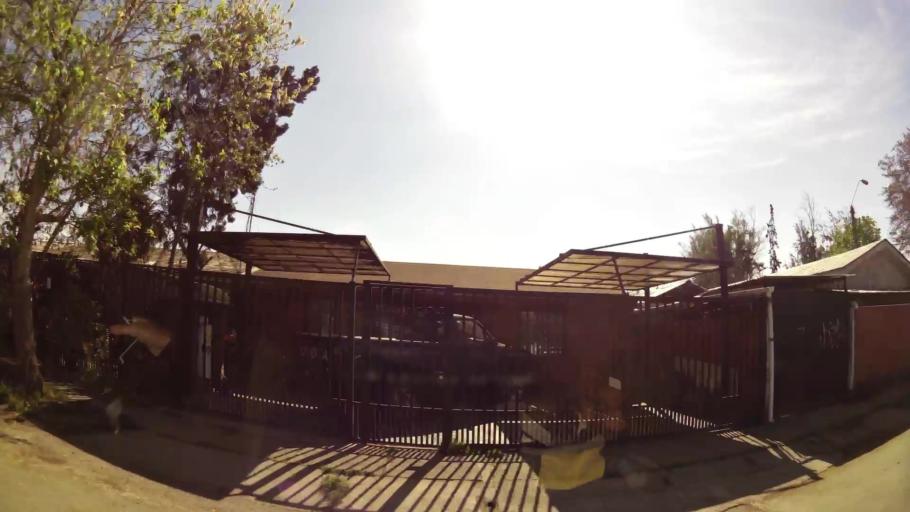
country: CL
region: Santiago Metropolitan
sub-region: Provincia de Santiago
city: Villa Presidente Frei, Nunoa, Santiago, Chile
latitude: -33.4989
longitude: -70.5820
